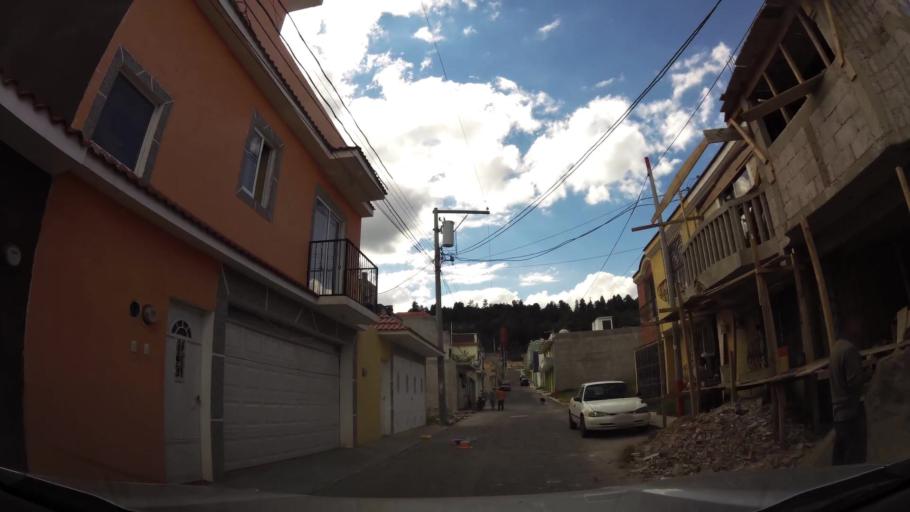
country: GT
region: Quetzaltenango
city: Quetzaltenango
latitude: 14.8355
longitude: -91.5498
